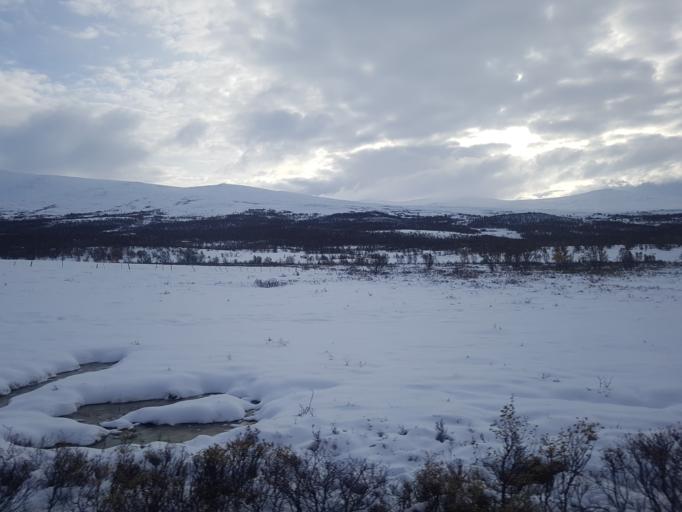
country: NO
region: Oppland
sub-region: Dovre
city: Dovre
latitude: 62.1184
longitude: 9.2893
